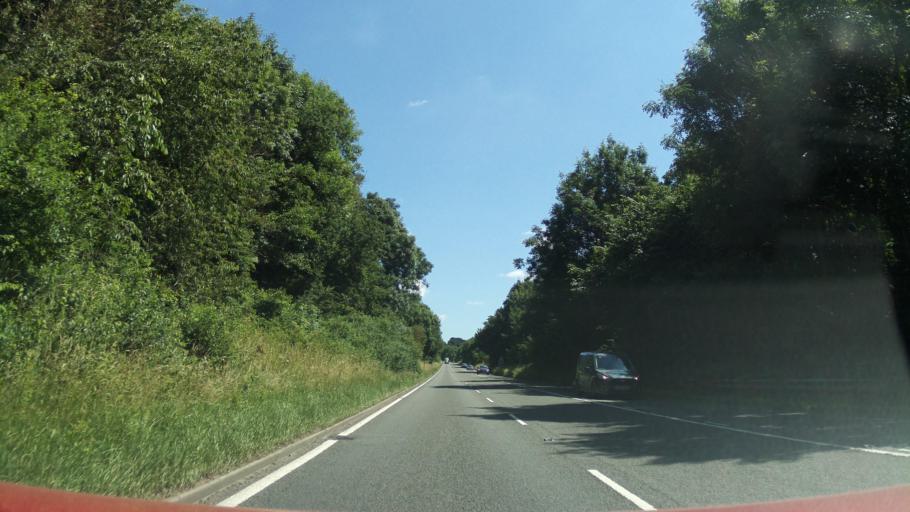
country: GB
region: England
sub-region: Derbyshire
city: Ashbourne
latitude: 53.0074
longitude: -1.7382
